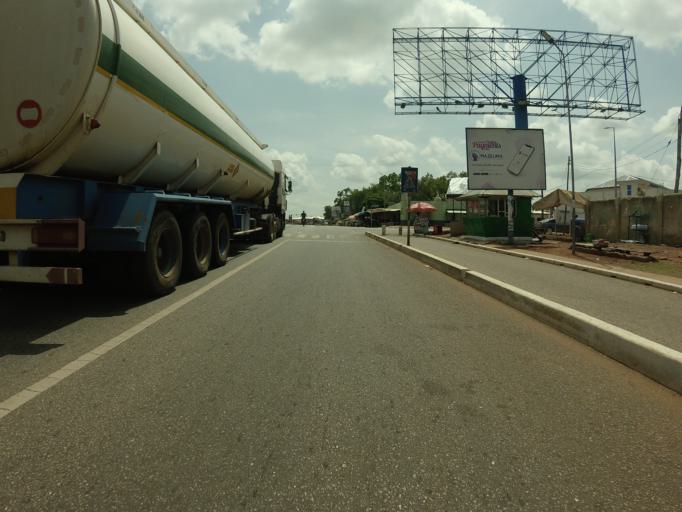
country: GH
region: Northern
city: Tamale
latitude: 9.4011
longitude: -0.8364
